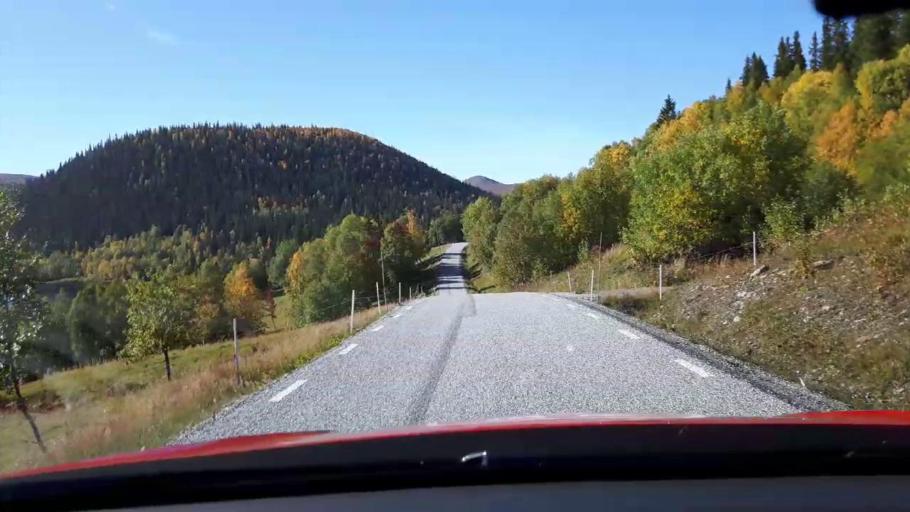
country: NO
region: Nord-Trondelag
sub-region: Royrvik
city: Royrvik
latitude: 64.8774
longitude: 14.2254
